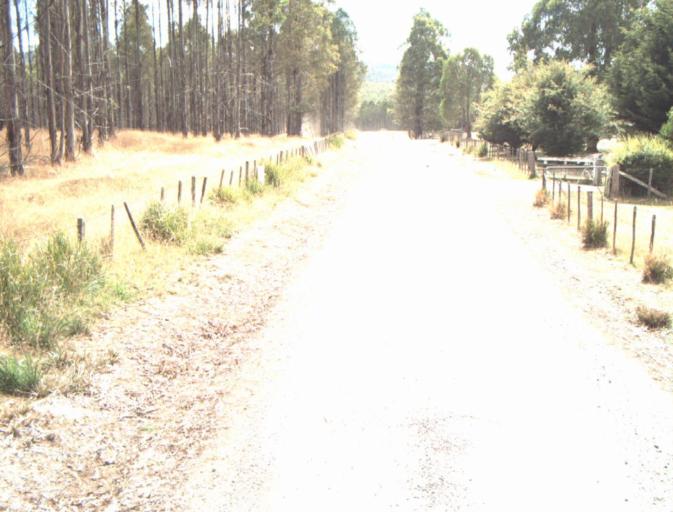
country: AU
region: Tasmania
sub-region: Dorset
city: Scottsdale
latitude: -41.4160
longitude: 147.5245
